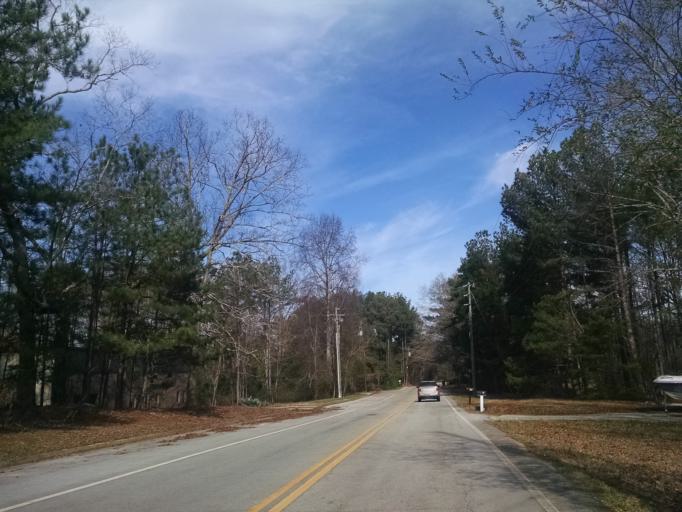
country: US
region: Georgia
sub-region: Gwinnett County
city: Sugar Hill
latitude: 34.0872
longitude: -84.0410
